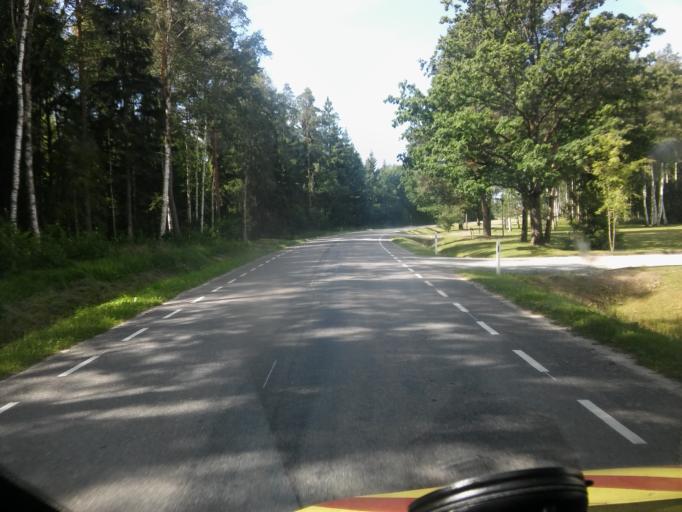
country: EE
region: Paernumaa
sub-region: Paikuse vald
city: Paikuse
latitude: 58.2408
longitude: 24.7212
